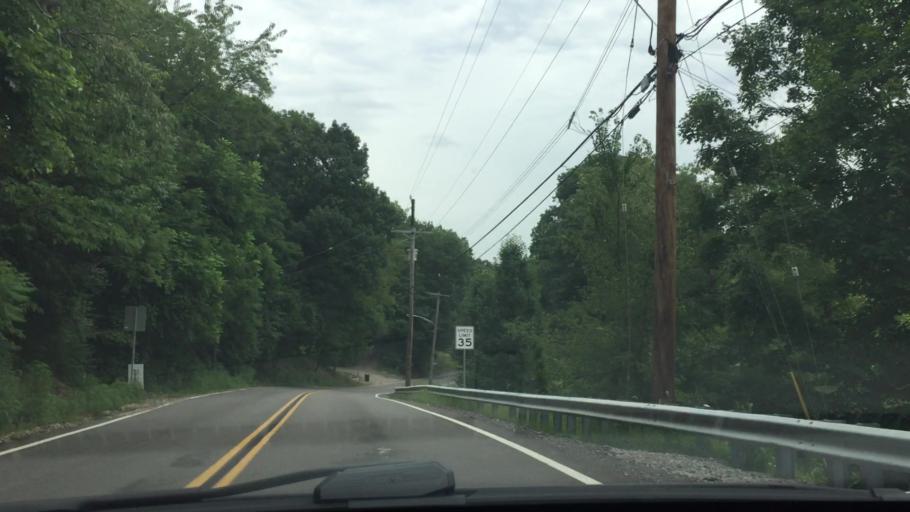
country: US
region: Pennsylvania
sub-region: Allegheny County
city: Rennerdale
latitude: 40.3925
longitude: -80.1599
